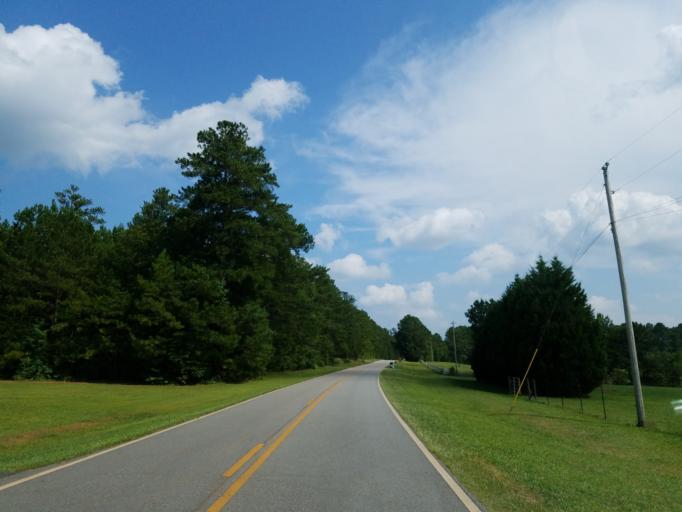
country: US
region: Georgia
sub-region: Monroe County
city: Forsyth
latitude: 33.0088
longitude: -83.8514
